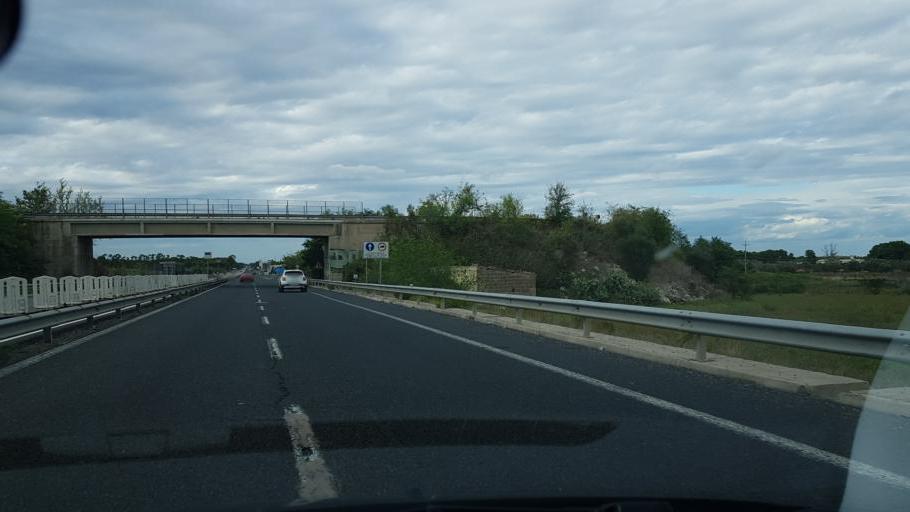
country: IT
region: Apulia
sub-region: Provincia di Lecce
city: San Donato di Lecce
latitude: 40.2763
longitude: 18.2036
